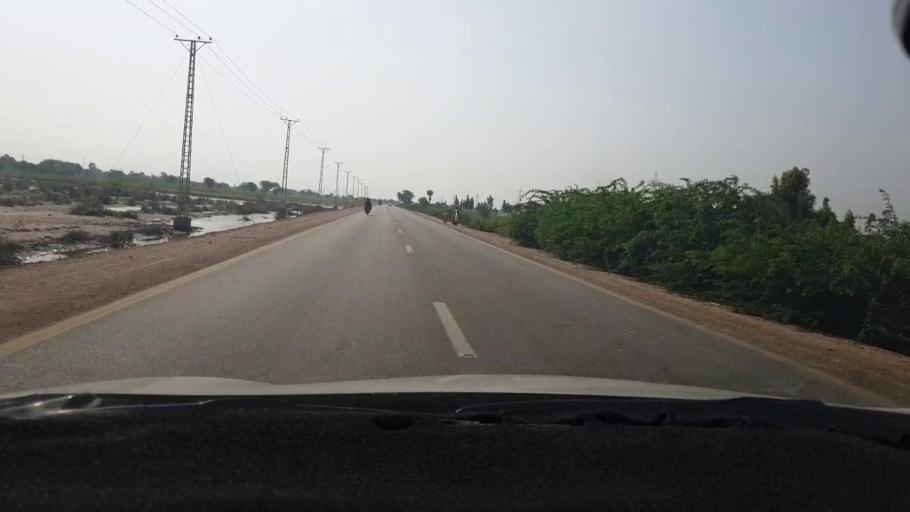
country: PK
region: Sindh
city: Jhol
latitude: 25.9372
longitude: 68.9899
